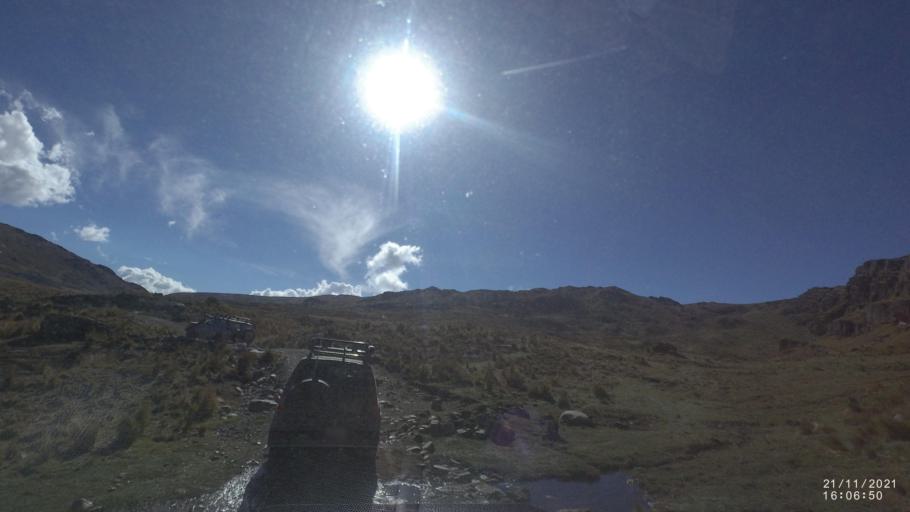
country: BO
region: Cochabamba
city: Cochabamba
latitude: -16.9911
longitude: -66.2642
